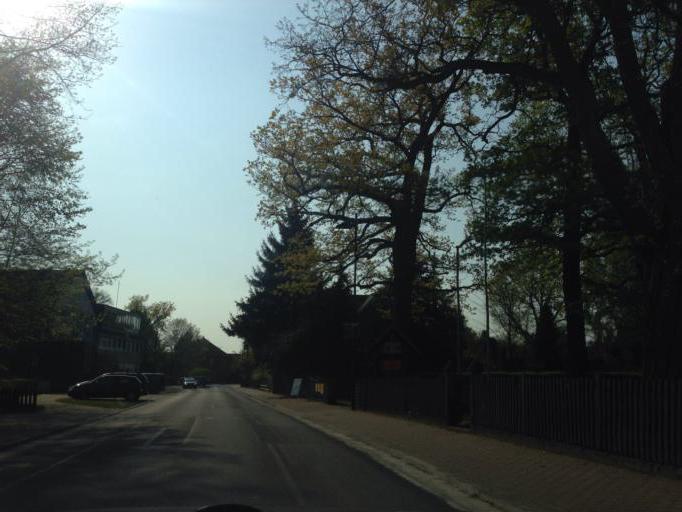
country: DE
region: Lower Saxony
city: Wathlingen
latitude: 52.5393
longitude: 10.1552
